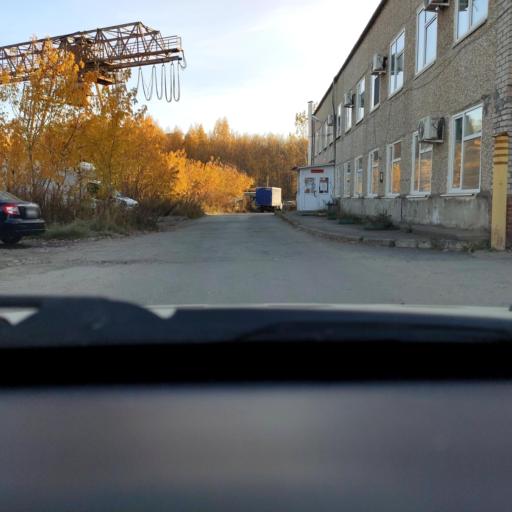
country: RU
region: Perm
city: Froly
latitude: 57.9638
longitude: 56.2732
